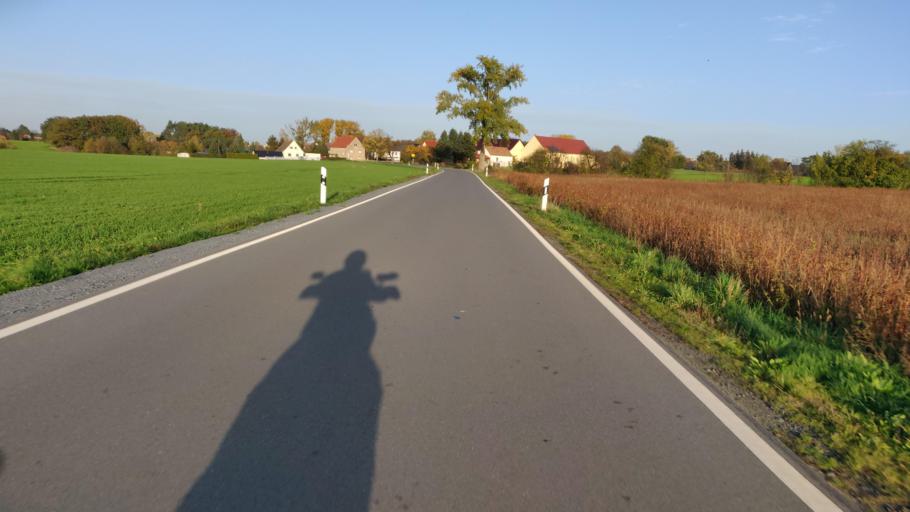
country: DE
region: Brandenburg
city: Hirschfeld
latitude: 51.3460
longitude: 13.6192
